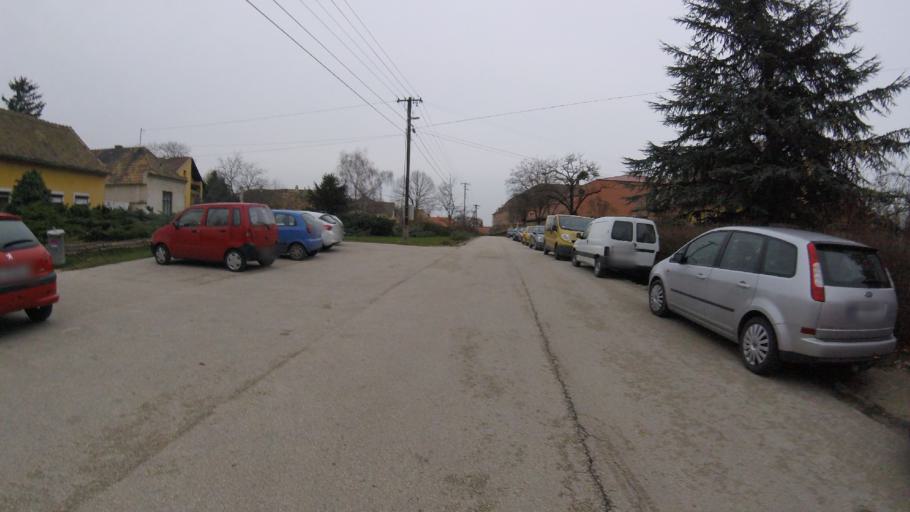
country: HU
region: Komarom-Esztergom
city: Tata
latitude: 47.6417
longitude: 18.3196
